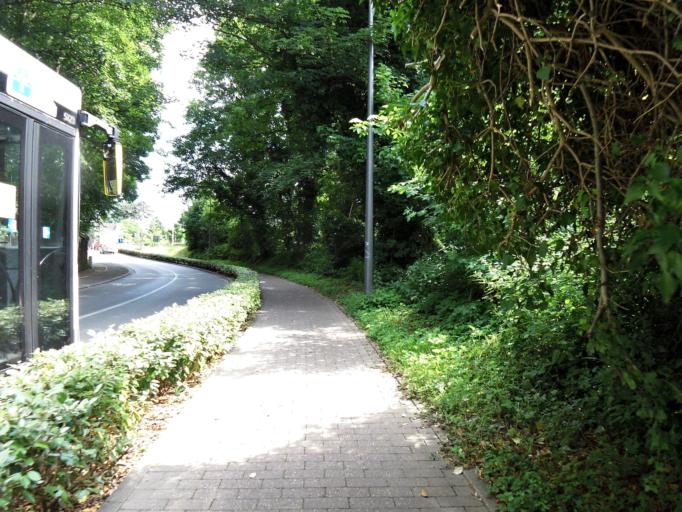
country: BE
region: Flanders
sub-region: Provincie Vlaams-Brabant
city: Dilbeek
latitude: 50.8513
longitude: 4.2621
